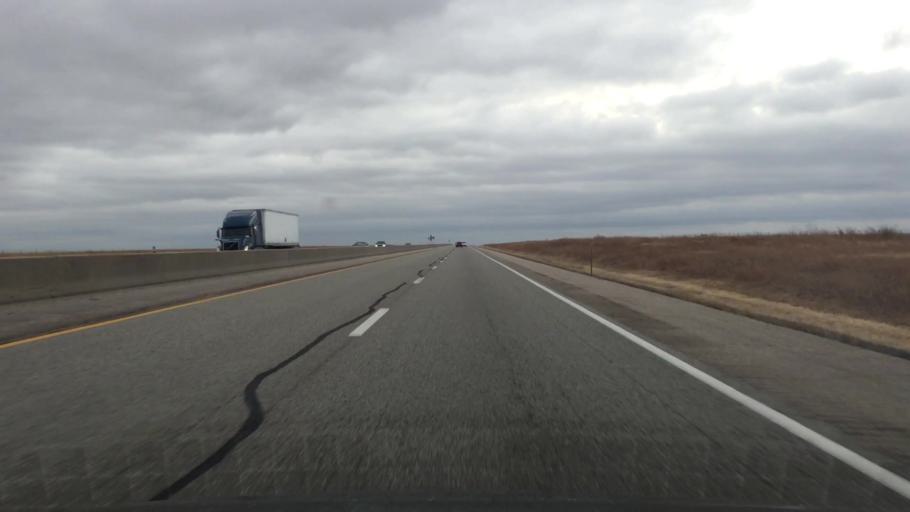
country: US
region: Kansas
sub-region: Butler County
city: El Dorado
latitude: 37.9097
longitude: -96.8134
